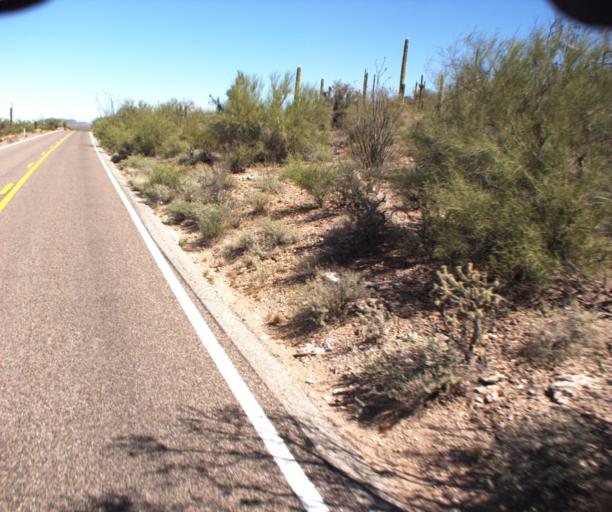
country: MX
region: Sonora
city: Sonoyta
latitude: 32.0175
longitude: -112.8037
